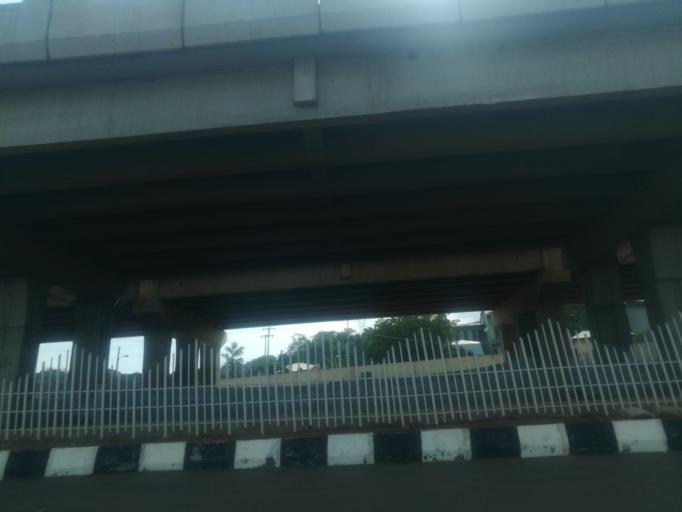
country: NG
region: Ogun
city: Abeokuta
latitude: 7.1260
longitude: 3.3575
